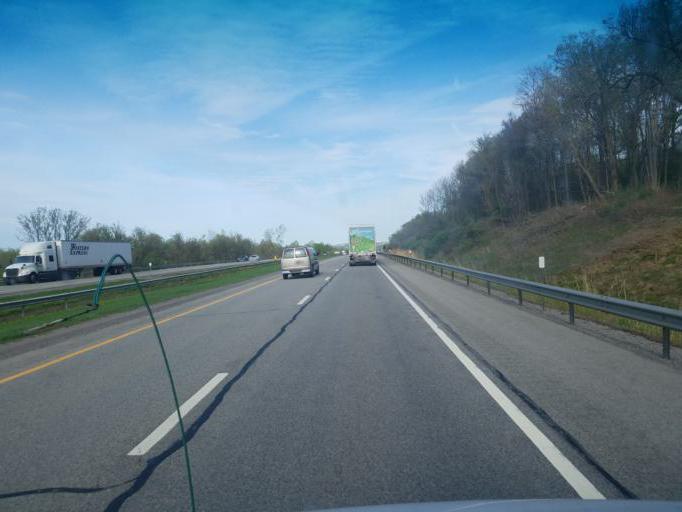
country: US
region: New York
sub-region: Herkimer County
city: Herkimer
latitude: 43.0143
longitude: -74.9639
